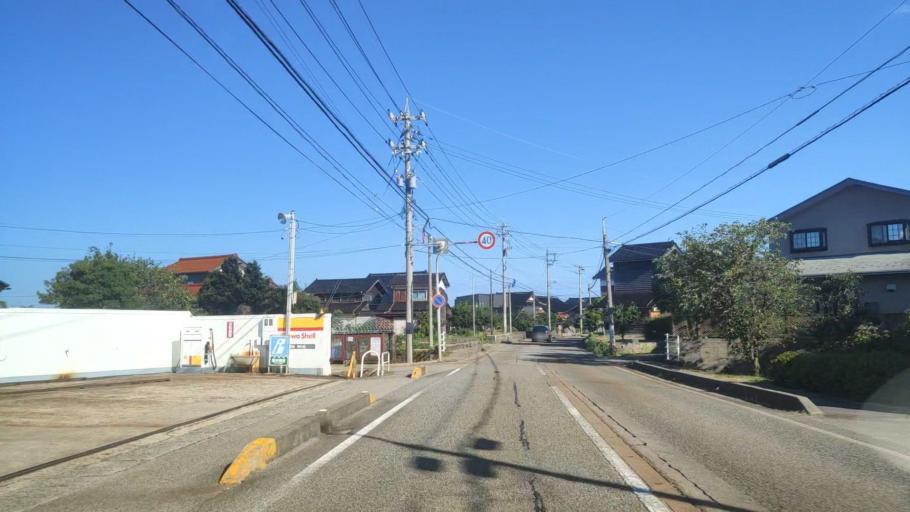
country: JP
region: Ishikawa
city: Hakui
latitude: 36.8210
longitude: 136.7568
